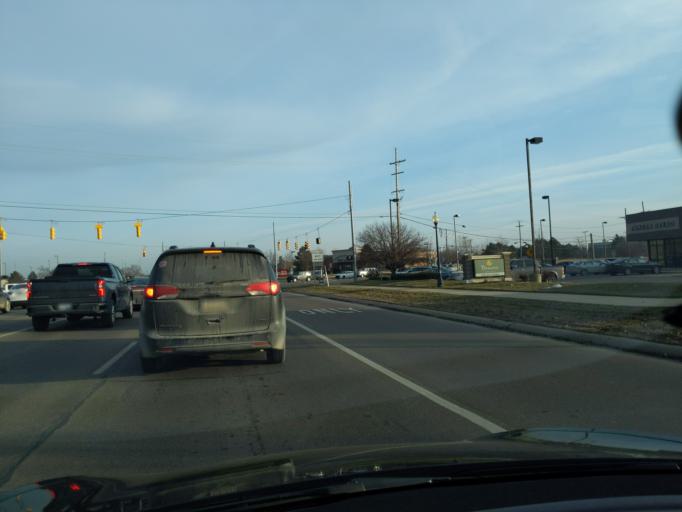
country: US
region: Michigan
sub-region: Livingston County
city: Howell
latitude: 42.5871
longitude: -83.8751
